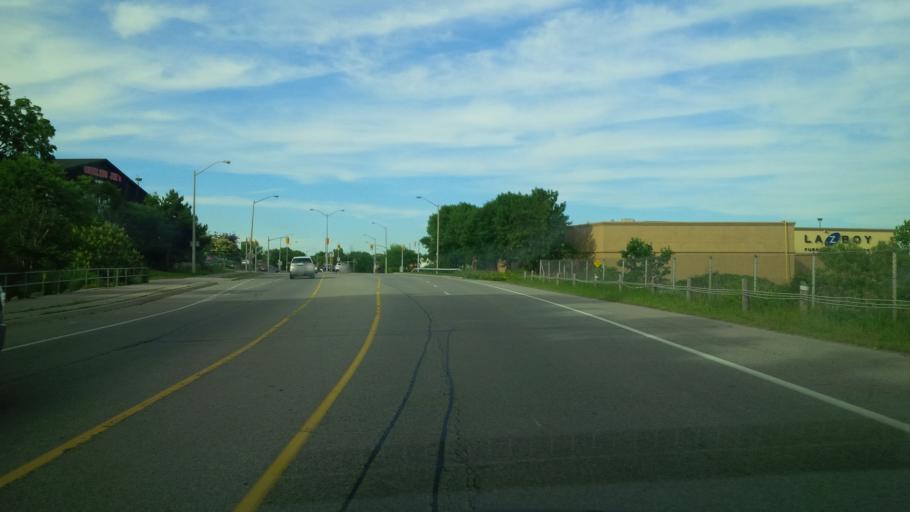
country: CA
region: Ontario
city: Burlington
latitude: 43.3415
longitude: -79.8281
